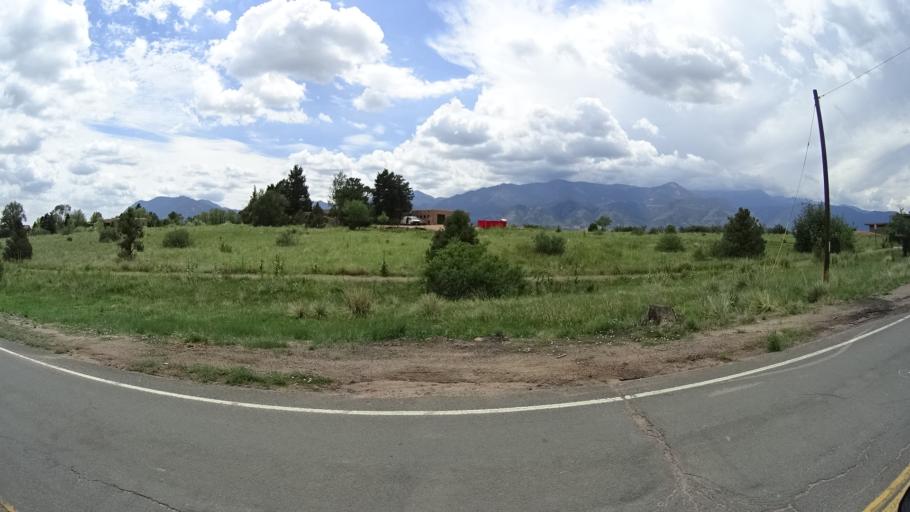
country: US
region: Colorado
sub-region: El Paso County
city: Colorado Springs
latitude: 38.8548
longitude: -104.8439
